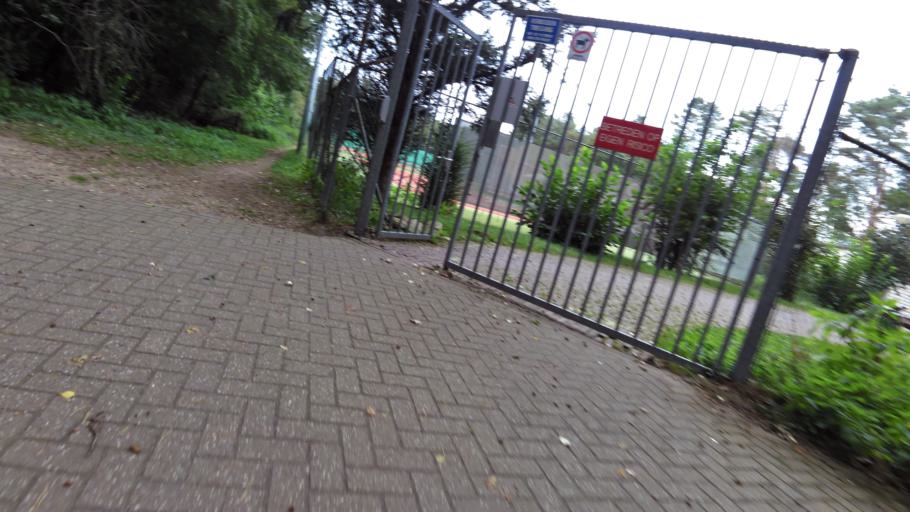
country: NL
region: Utrecht
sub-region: Gemeente Utrechtse Heuvelrug
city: Leersum
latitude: 52.0186
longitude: 5.4358
